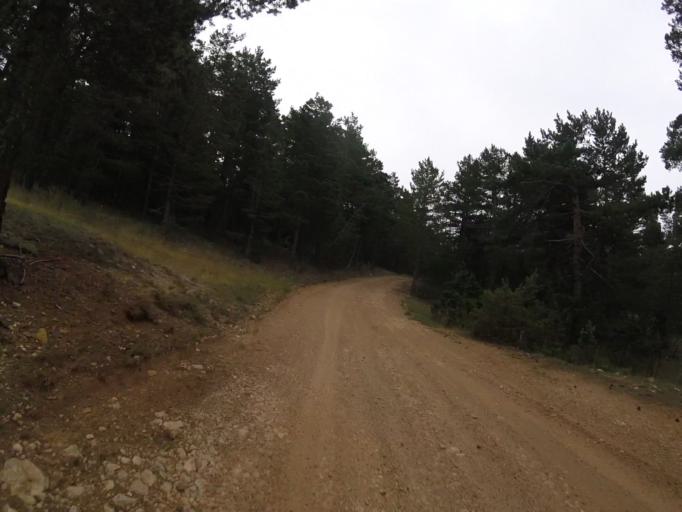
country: ES
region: Aragon
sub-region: Provincia de Teruel
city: Valdelinares
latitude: 40.3650
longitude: -0.6173
